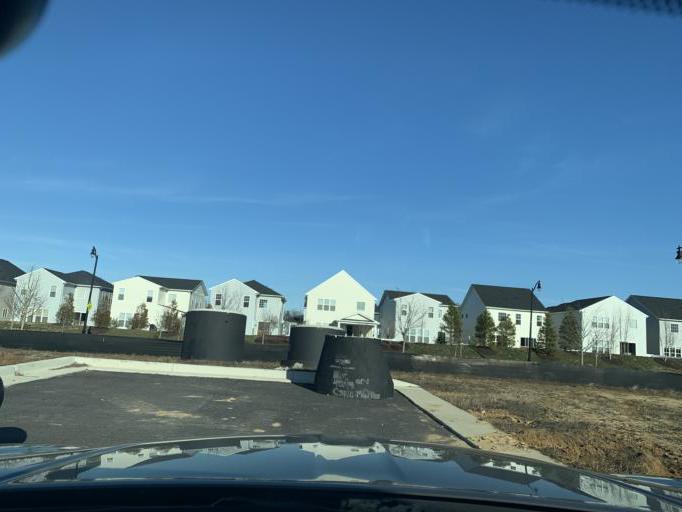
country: US
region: Maryland
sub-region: Anne Arundel County
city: Crofton
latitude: 39.0207
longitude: -76.7234
